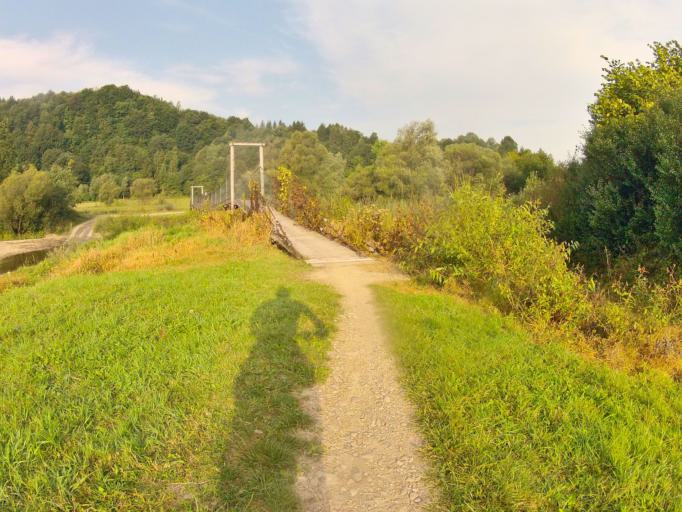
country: PL
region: Subcarpathian Voivodeship
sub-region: Powiat jasielski
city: Nowy Zmigrod
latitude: 49.5538
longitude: 21.5391
